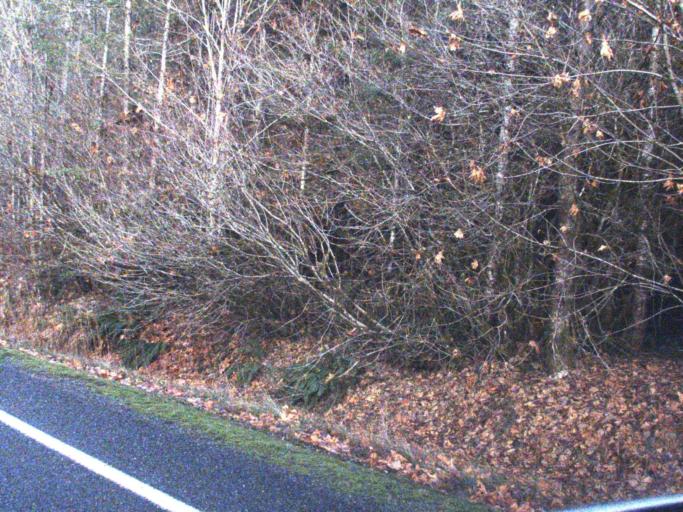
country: US
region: Washington
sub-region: Snohomish County
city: Darrington
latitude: 48.3970
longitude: -121.5508
